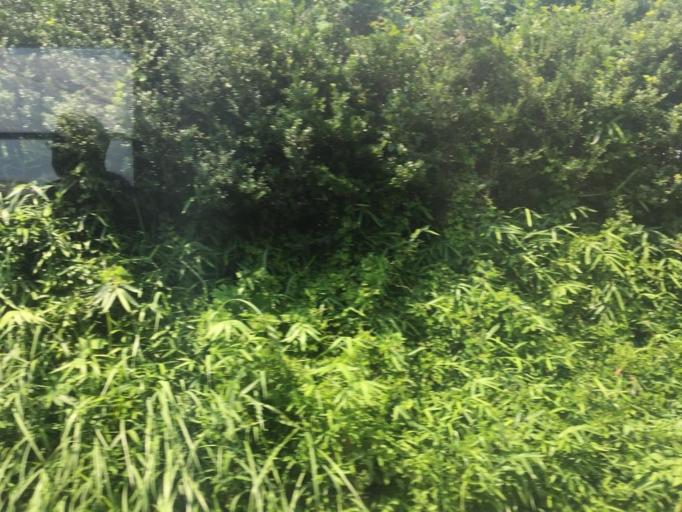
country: JP
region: Gunma
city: Maebashi-shi
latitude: 36.4045
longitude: 139.1274
